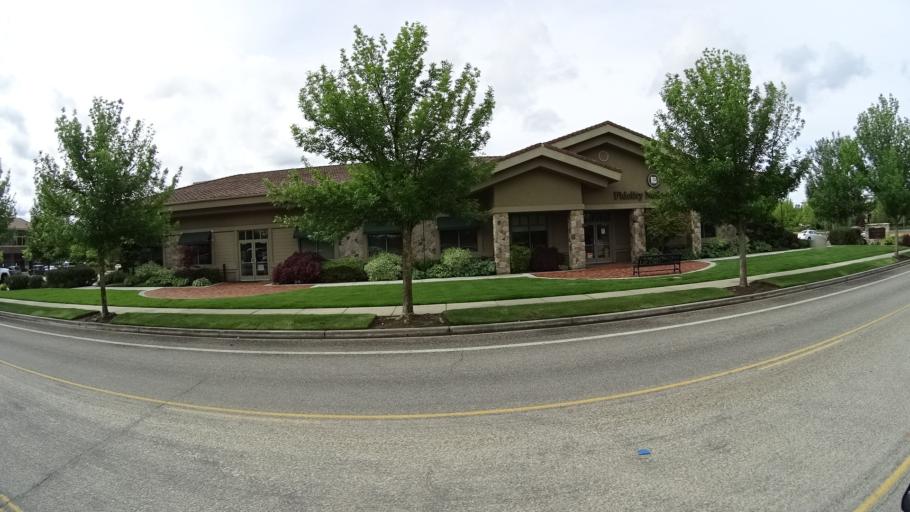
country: US
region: Idaho
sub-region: Ada County
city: Eagle
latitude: 43.6894
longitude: -116.3479
